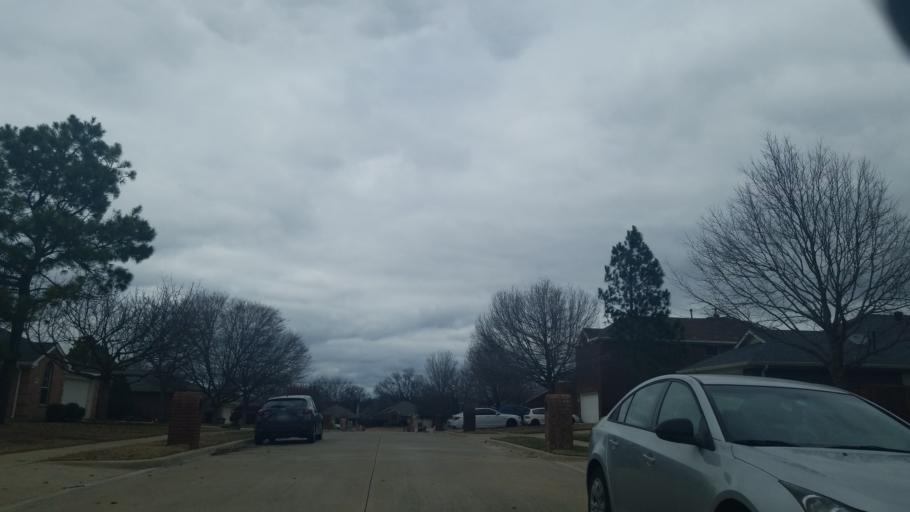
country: US
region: Texas
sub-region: Denton County
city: Corinth
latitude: 33.1339
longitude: -97.0890
